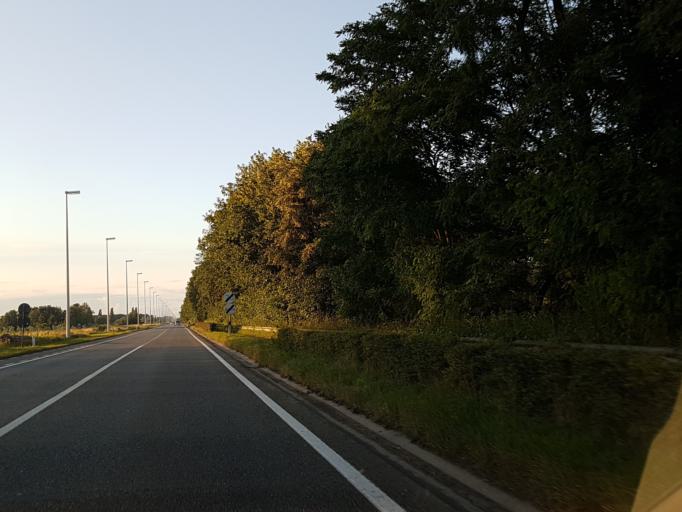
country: BE
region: Flanders
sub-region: Provincie Oost-Vlaanderen
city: Dendermonde
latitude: 51.0457
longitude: 4.1212
